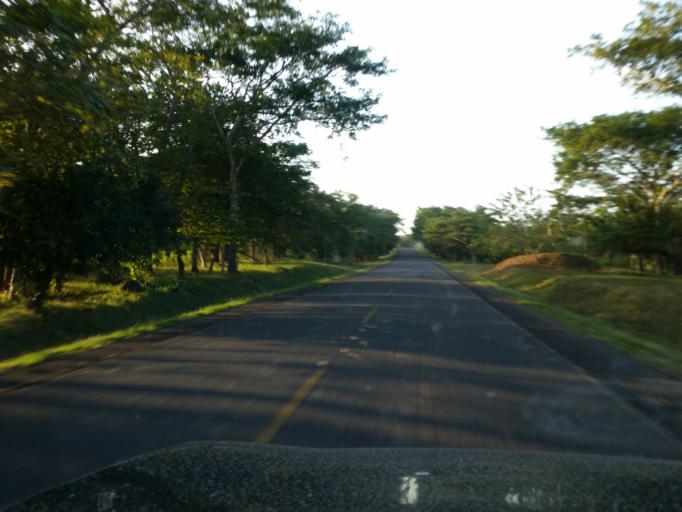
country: NI
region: Rio San Juan
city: El Almendro
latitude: 11.6044
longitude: -84.8634
